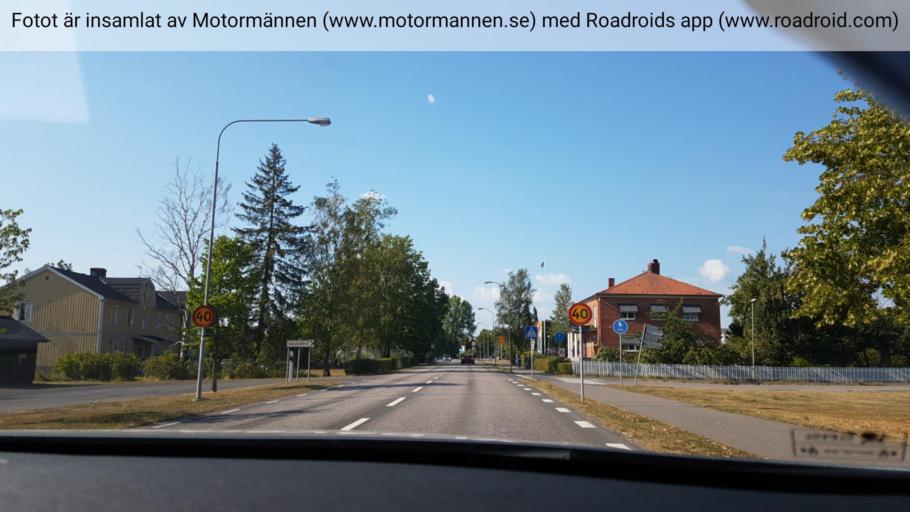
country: SE
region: Vaestra Goetaland
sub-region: Skovde Kommun
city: Stopen
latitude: 58.5734
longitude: 14.0048
